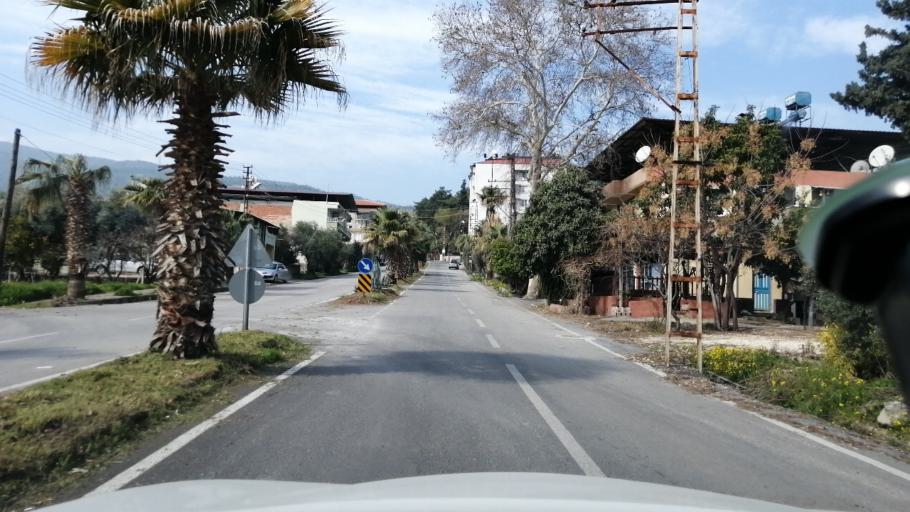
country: TR
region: Hatay
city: Serinyol
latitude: 36.3532
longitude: 36.2087
